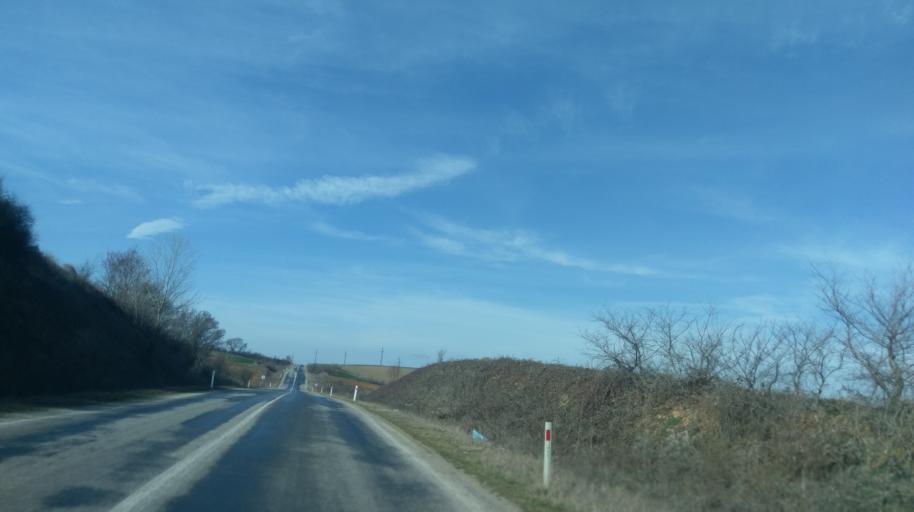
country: TR
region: Edirne
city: Uzun Keupru
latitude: 41.2759
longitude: 26.7492
